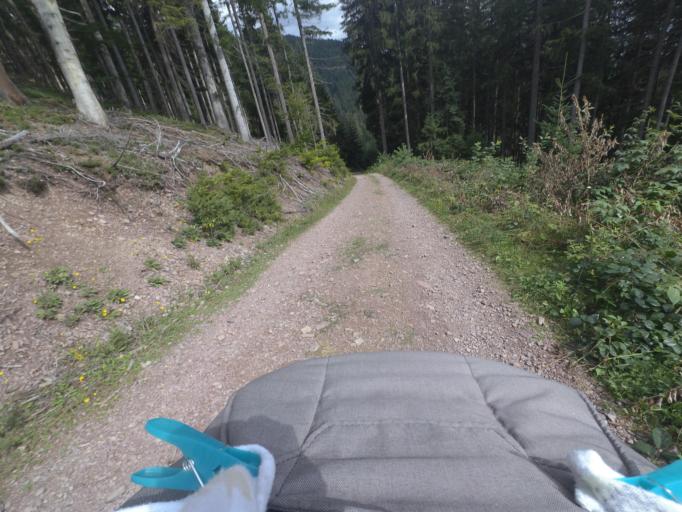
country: AT
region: Salzburg
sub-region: Politischer Bezirk Sankt Johann im Pongau
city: Werfenweng
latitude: 47.4712
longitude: 13.2386
